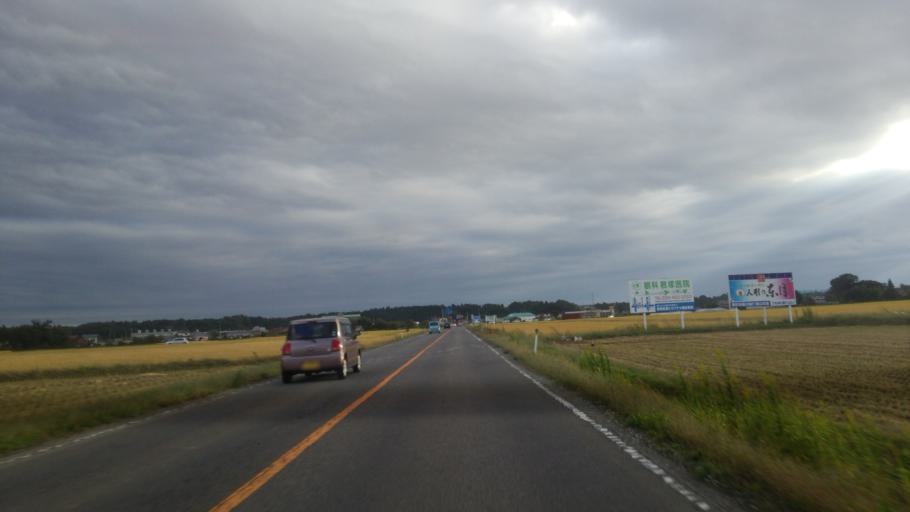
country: JP
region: Fukushima
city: Koriyama
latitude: 37.3700
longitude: 140.3406
